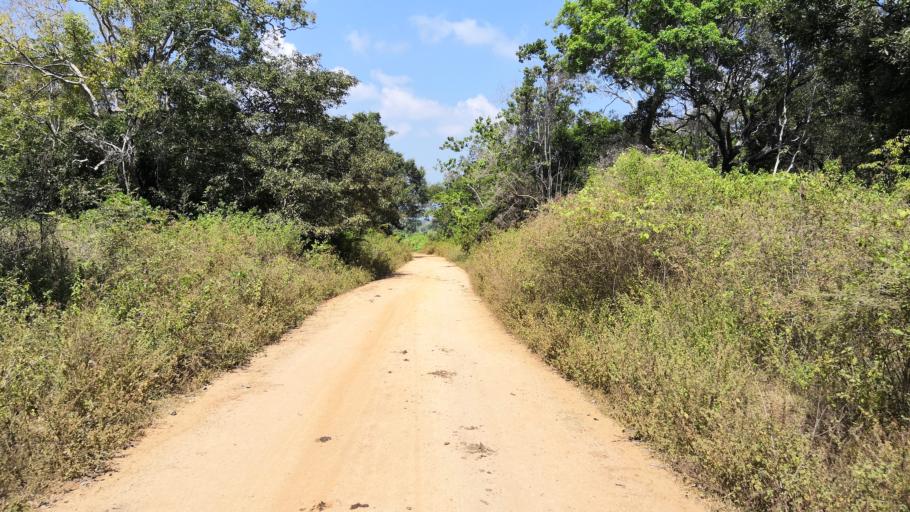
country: LK
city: Padaviya Divisional Secretariat
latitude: 8.9723
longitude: 80.6852
